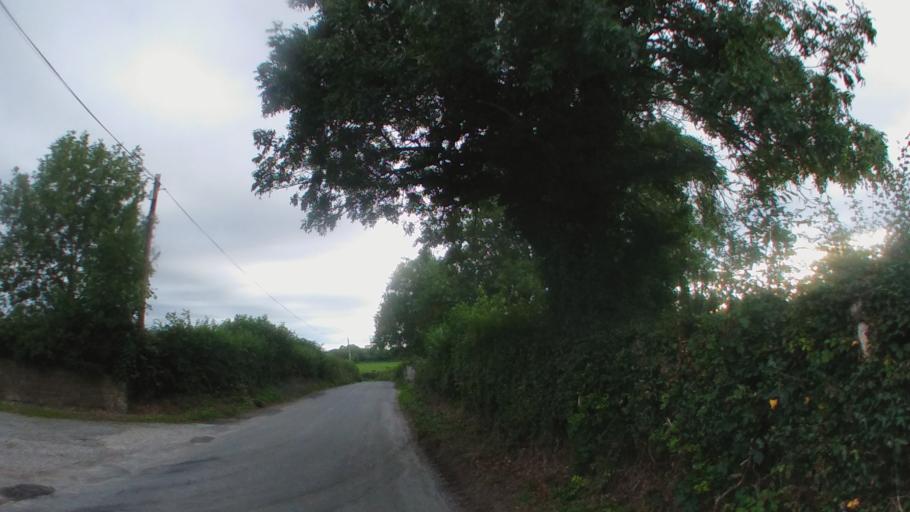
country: IE
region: Leinster
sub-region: Kilkenny
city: Kilkenny
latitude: 52.6898
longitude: -7.2169
